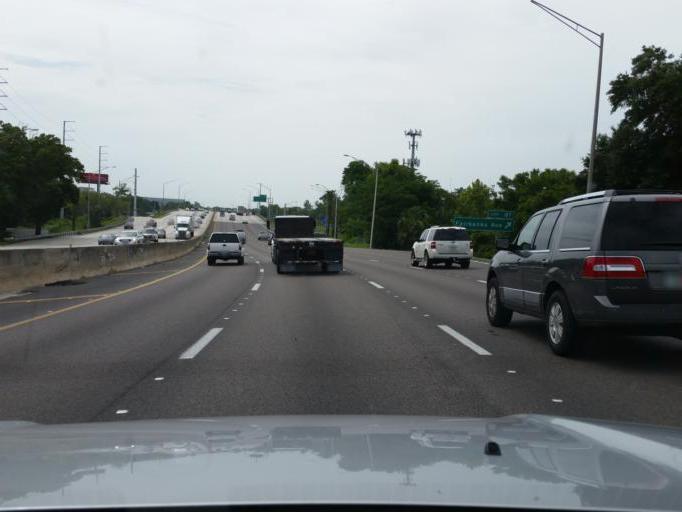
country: US
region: Florida
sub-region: Orange County
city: Fairview Shores
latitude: 28.5958
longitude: -81.3853
